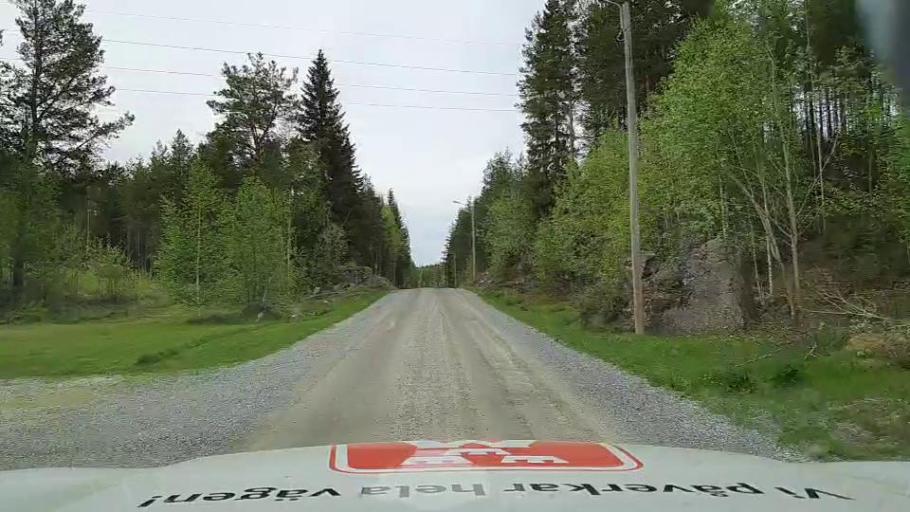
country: SE
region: Jaemtland
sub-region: Braecke Kommun
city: Braecke
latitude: 62.4572
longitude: 14.9162
